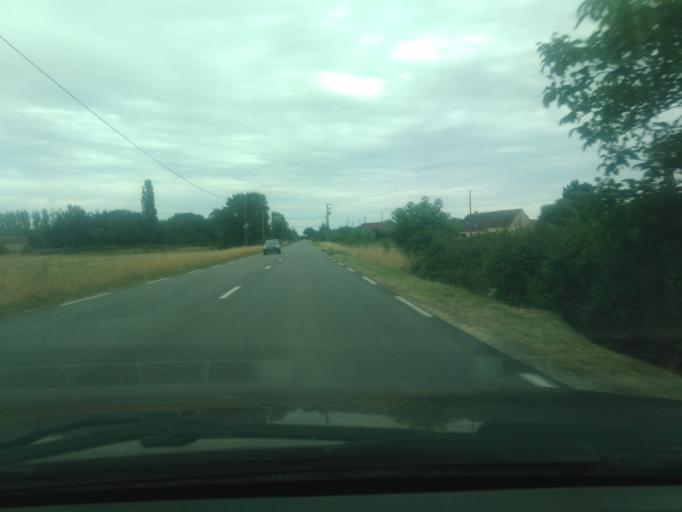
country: FR
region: Centre
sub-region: Departement du Cher
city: Charenton-du-Cher
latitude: 46.7312
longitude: 2.6177
